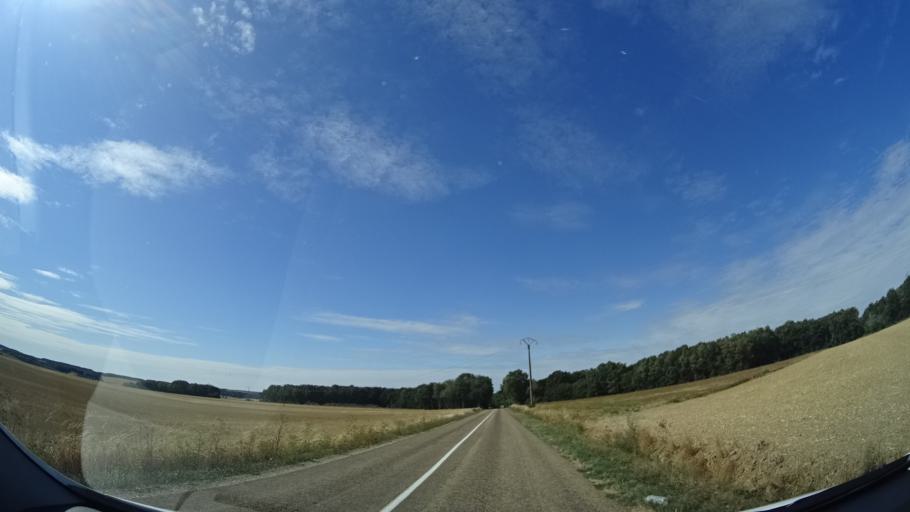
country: FR
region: Bourgogne
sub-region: Departement de l'Yonne
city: Cezy
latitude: 47.9355
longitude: 3.2617
